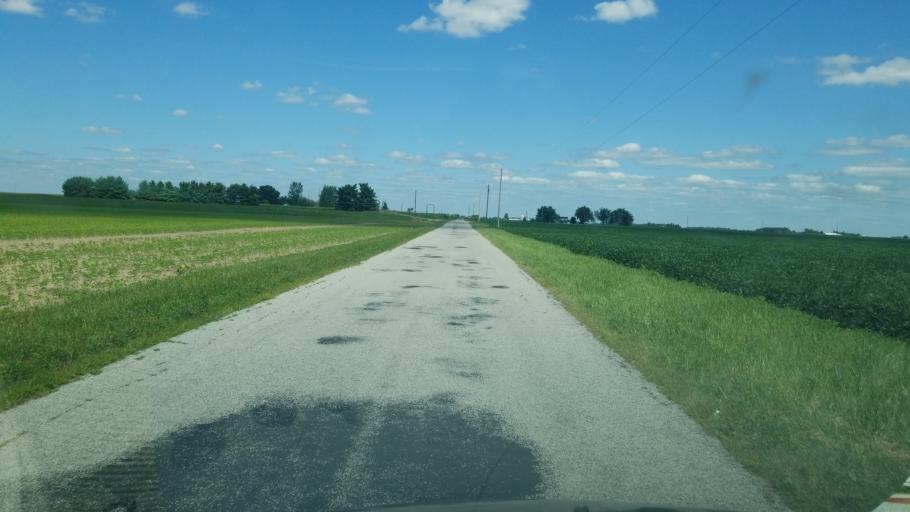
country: US
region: Ohio
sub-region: Fulton County
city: Delta
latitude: 41.6655
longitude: -84.0163
